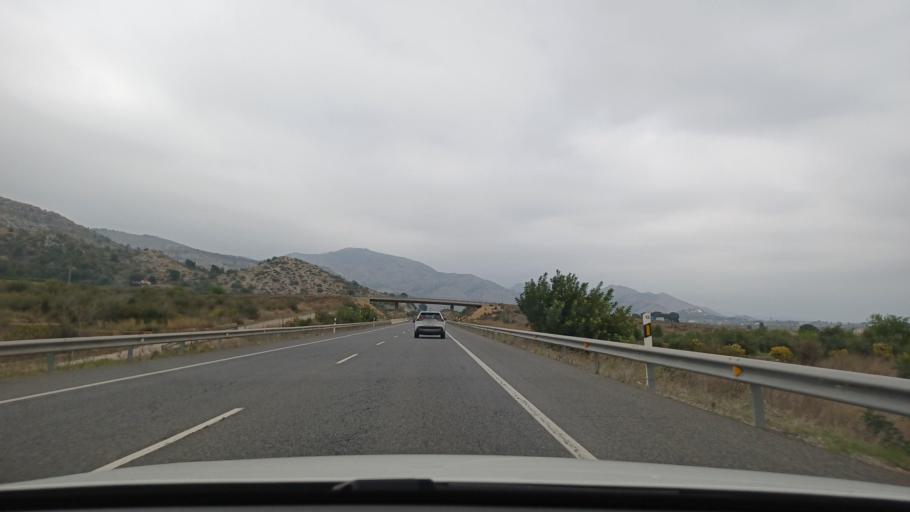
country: ES
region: Valencia
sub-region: Provincia de Castello
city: Borriol
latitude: 40.0205
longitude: -0.0407
